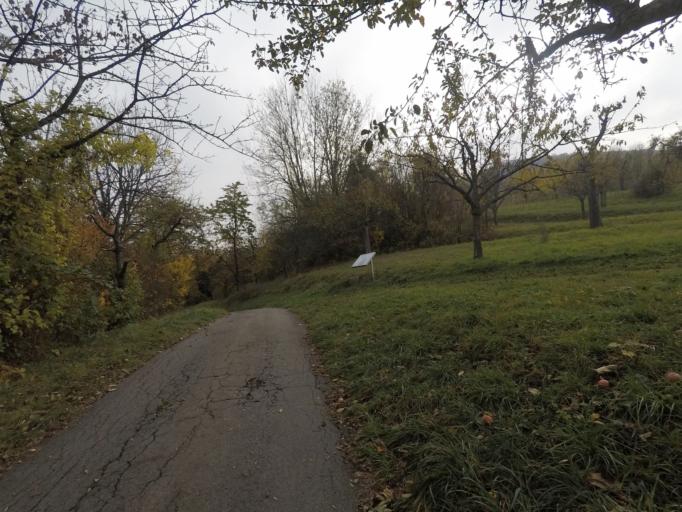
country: DE
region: Baden-Wuerttemberg
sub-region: Tuebingen Region
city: Pfullingen
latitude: 48.4532
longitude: 9.2272
